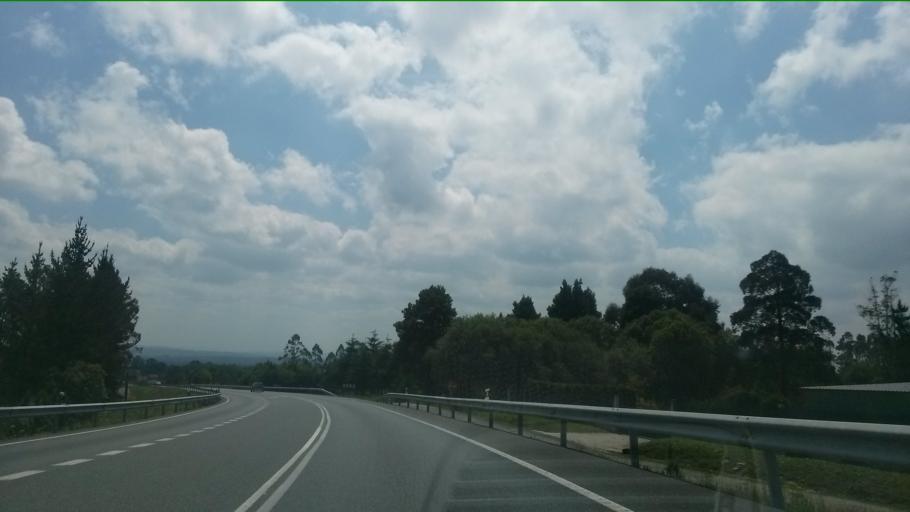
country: ES
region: Galicia
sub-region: Provincia da Coruna
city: Vilasantar
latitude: 43.0971
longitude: -8.1764
